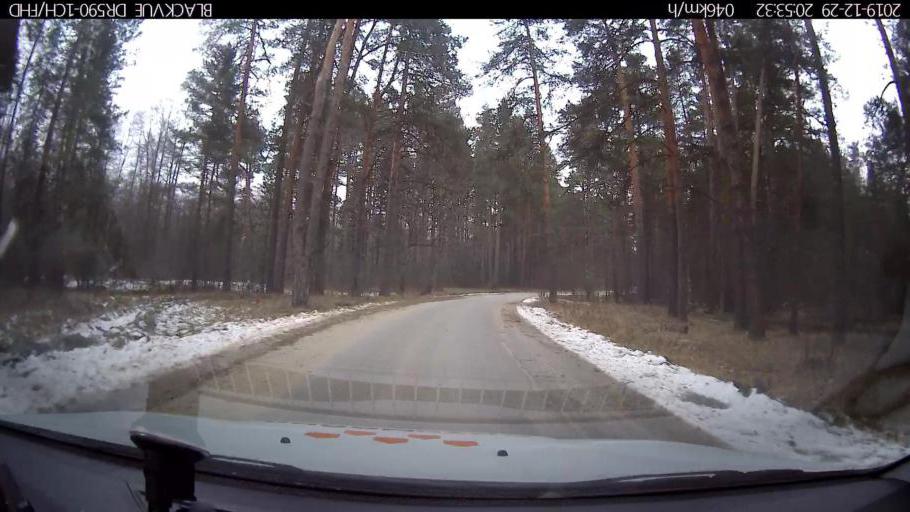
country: RU
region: Nizjnij Novgorod
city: Afonino
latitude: 56.1704
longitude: 43.9871
